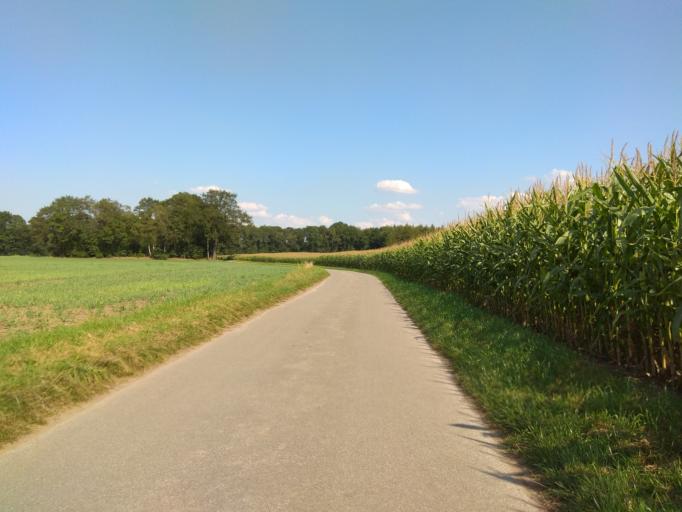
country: DE
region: North Rhine-Westphalia
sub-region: Regierungsbezirk Munster
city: Klein Reken
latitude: 51.7437
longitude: 7.0396
